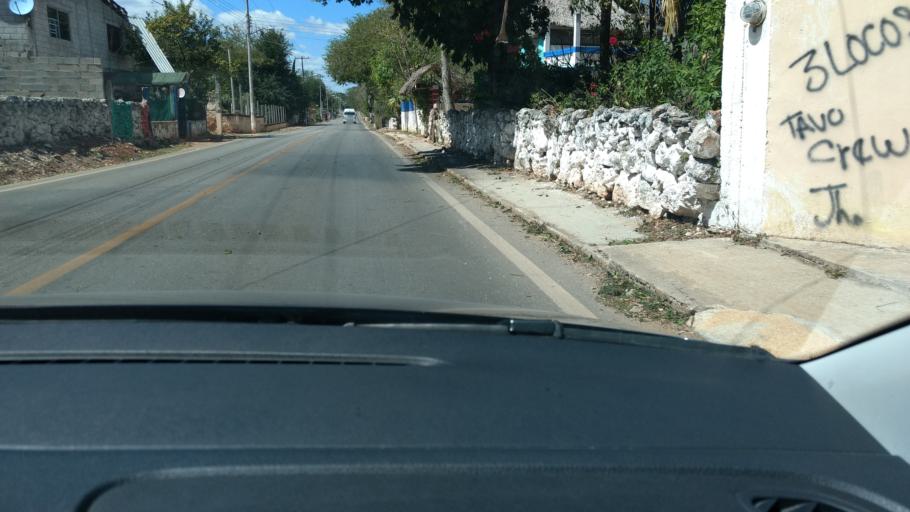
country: MX
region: Yucatan
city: Tzucacab
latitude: 20.0758
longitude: -89.0581
